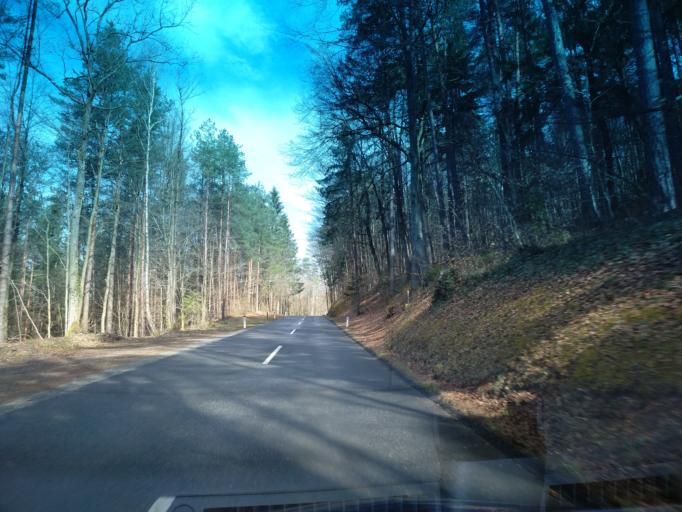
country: AT
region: Styria
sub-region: Politischer Bezirk Leibnitz
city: Kitzeck im Sausal
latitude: 46.7663
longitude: 15.4453
